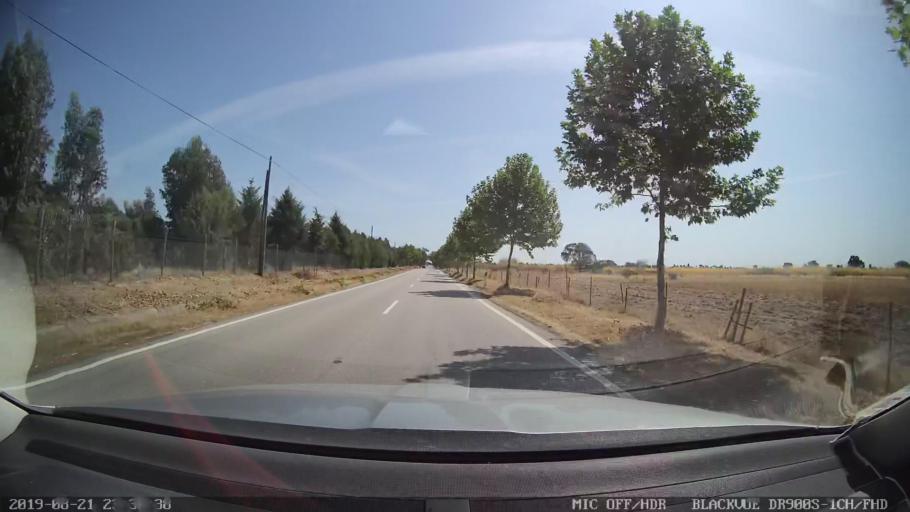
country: PT
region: Guarda
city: Alcains
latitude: 39.8704
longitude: -7.4443
